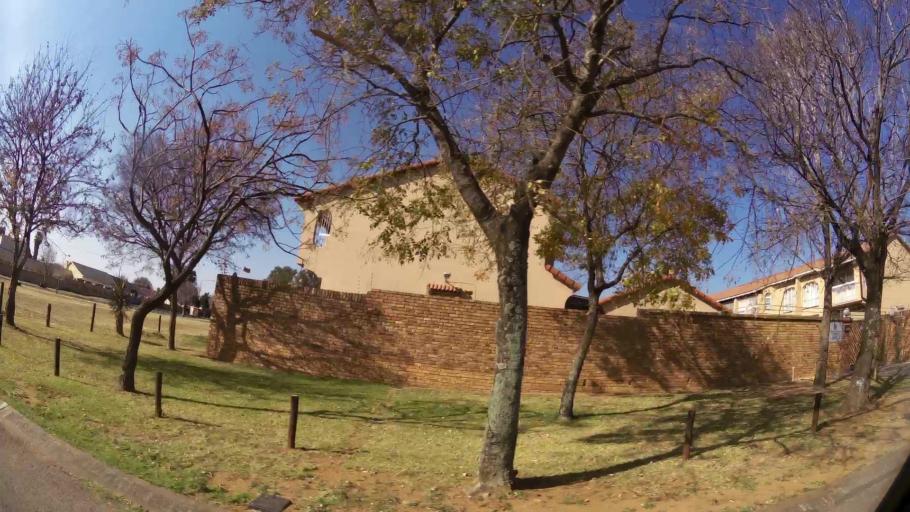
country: ZA
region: Gauteng
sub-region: City of Johannesburg Metropolitan Municipality
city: Johannesburg
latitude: -26.2579
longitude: 27.9942
